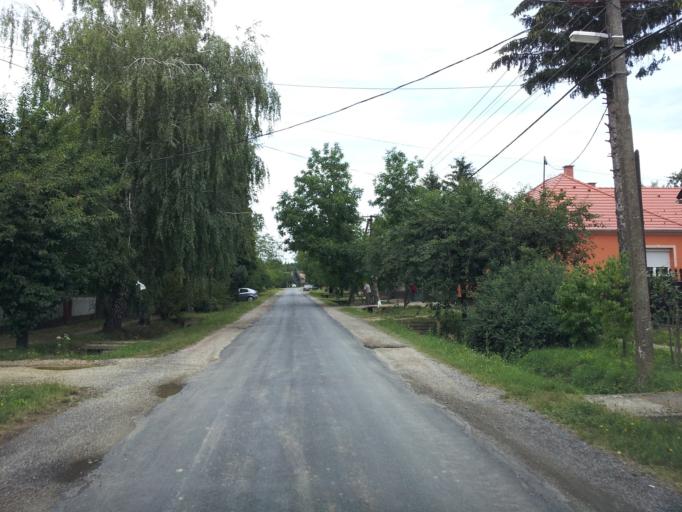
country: HU
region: Vas
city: Vasvar
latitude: 47.0480
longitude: 16.8737
